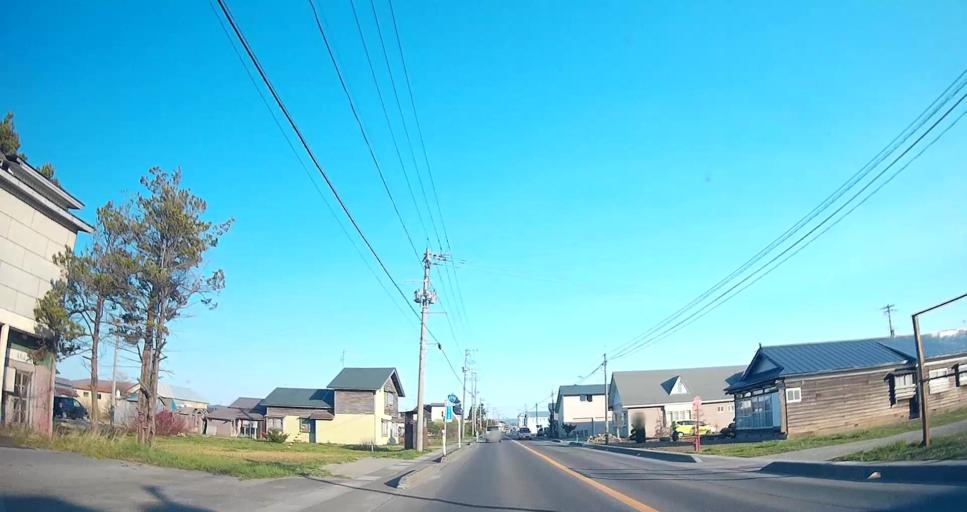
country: JP
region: Aomori
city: Mutsu
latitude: 41.2762
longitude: 141.2132
